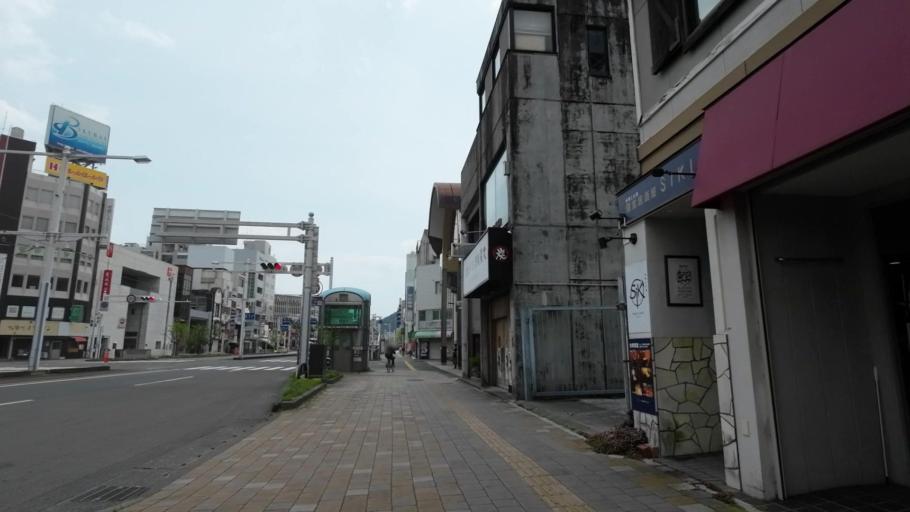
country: JP
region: Kochi
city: Kochi-shi
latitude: 33.5613
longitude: 133.5430
